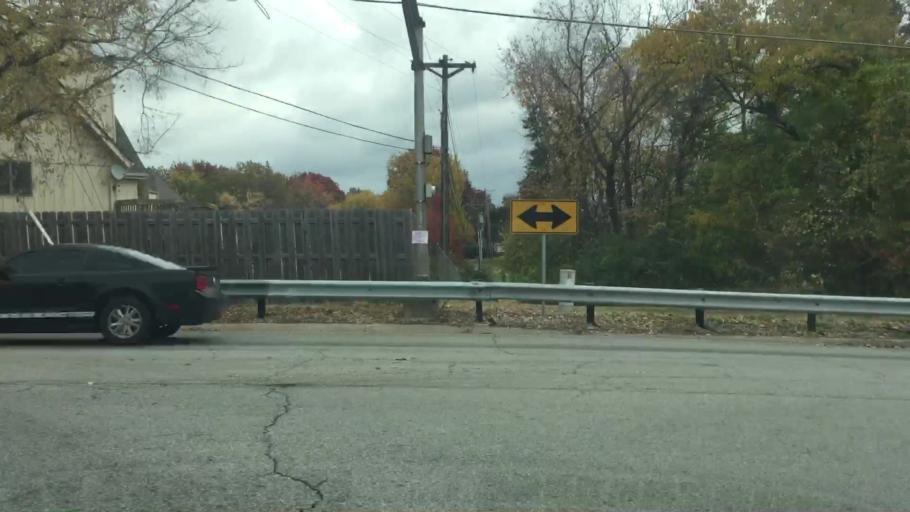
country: US
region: Missouri
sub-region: Jackson County
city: Raytown
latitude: 39.0080
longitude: -94.4450
